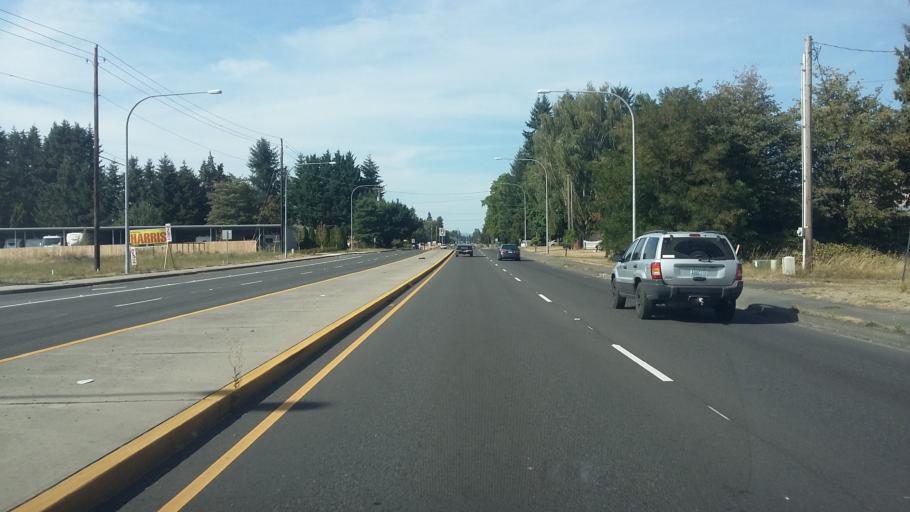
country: US
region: Washington
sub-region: Clark County
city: Brush Prairie
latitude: 45.7096
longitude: -122.5527
